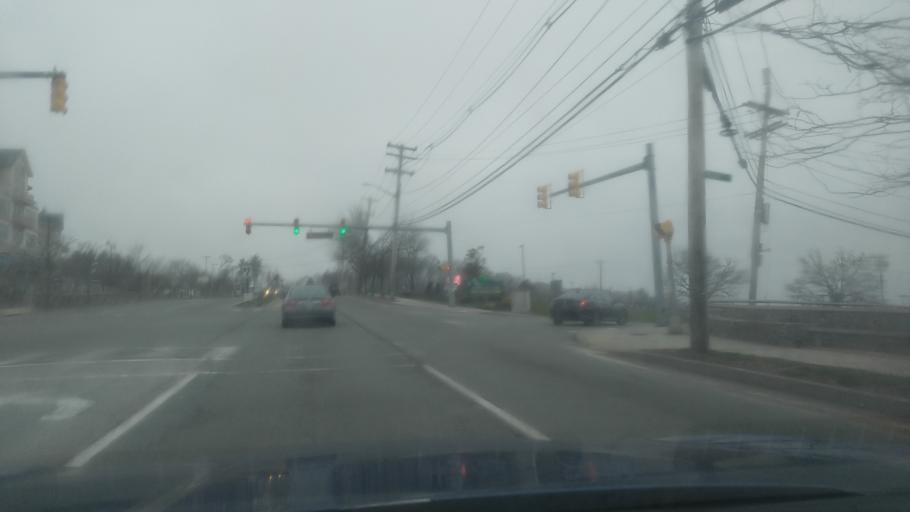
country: US
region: Rhode Island
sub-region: Providence County
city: Cranston
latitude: 41.7566
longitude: -71.4583
